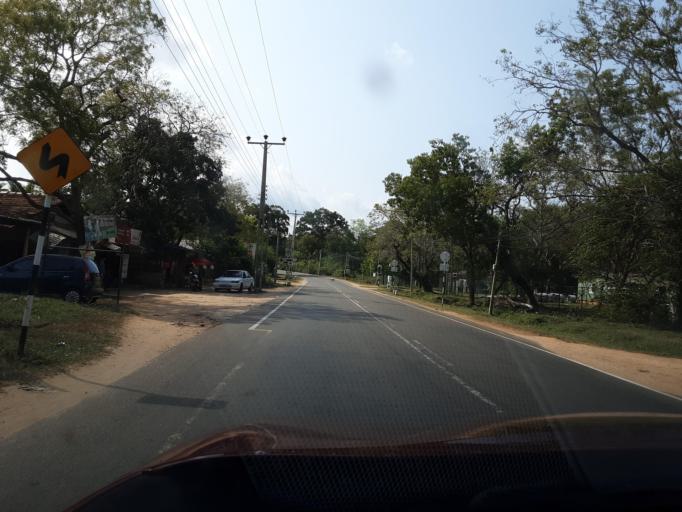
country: LK
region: Uva
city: Haputale
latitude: 6.3444
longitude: 81.2010
